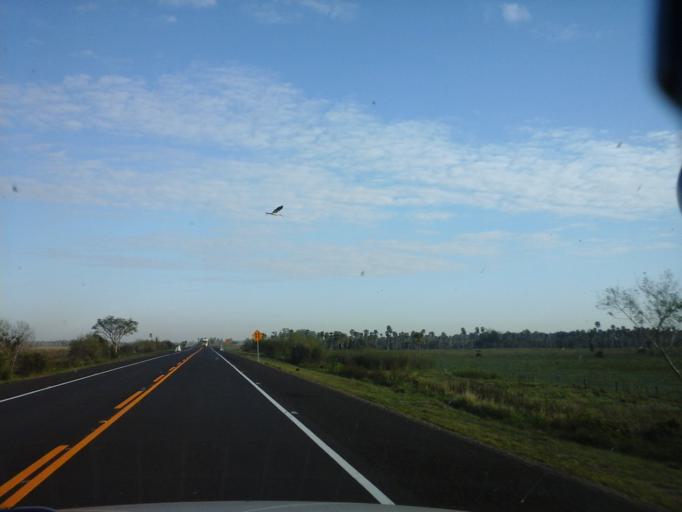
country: PY
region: Neembucu
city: Cerrito
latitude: -26.8849
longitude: -57.7356
